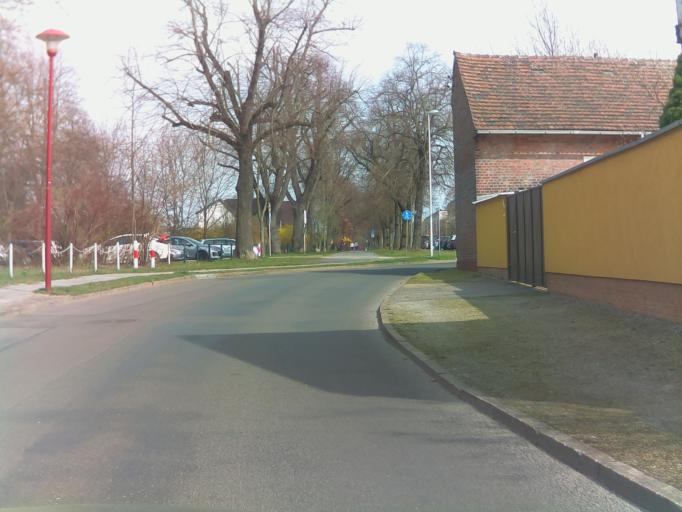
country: DE
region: Brandenburg
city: Cottbus
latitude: 51.7590
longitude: 14.3016
